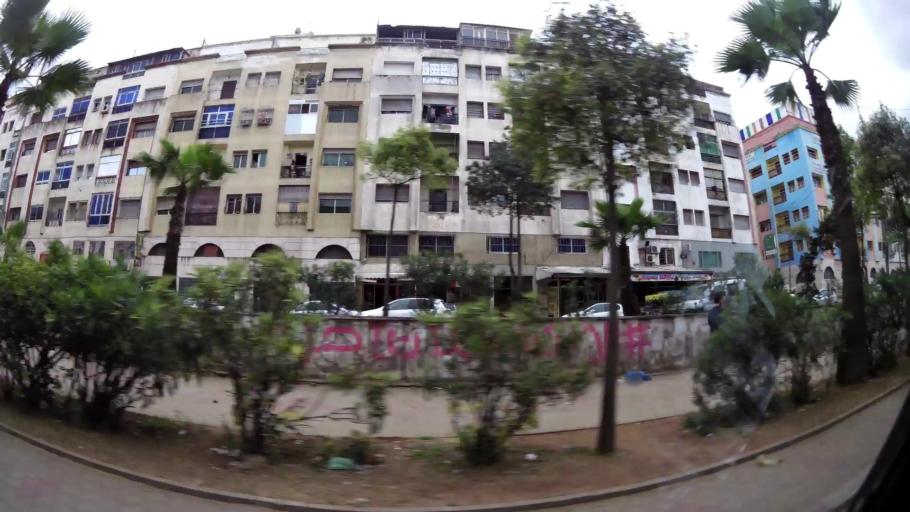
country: MA
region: Grand Casablanca
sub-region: Mediouna
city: Tit Mellil
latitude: 33.5620
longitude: -7.5501
